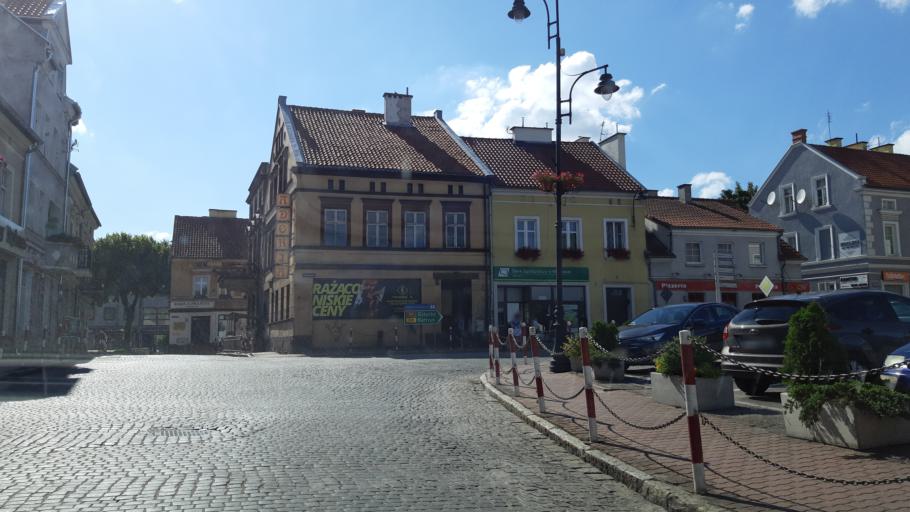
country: PL
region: Warmian-Masurian Voivodeship
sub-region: Powiat mragowski
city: Mragowo
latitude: 53.8713
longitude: 21.3042
